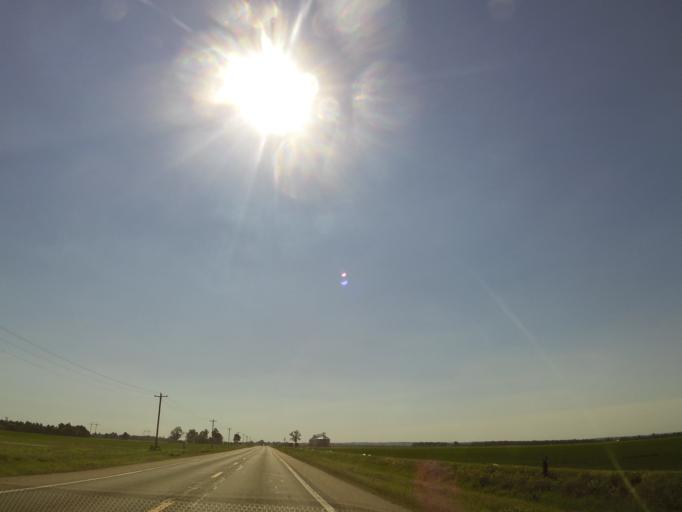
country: US
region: Arkansas
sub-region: Clay County
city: Corning
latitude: 36.4351
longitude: -90.4400
